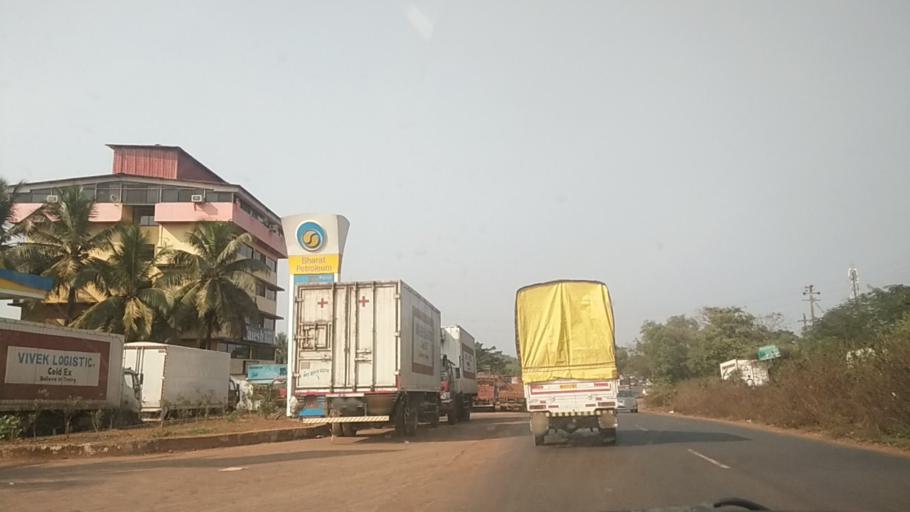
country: IN
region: Goa
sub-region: North Goa
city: Colovale
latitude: 15.6141
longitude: 73.8226
